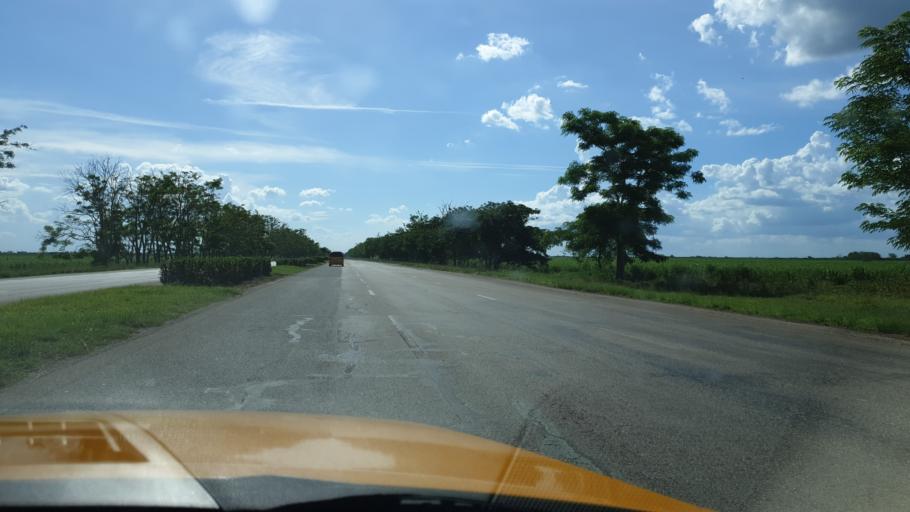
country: CU
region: Cienfuegos
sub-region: Municipio de Aguada de Pasajeros
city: Aguada de Pasajeros
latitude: 22.4117
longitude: -80.8959
